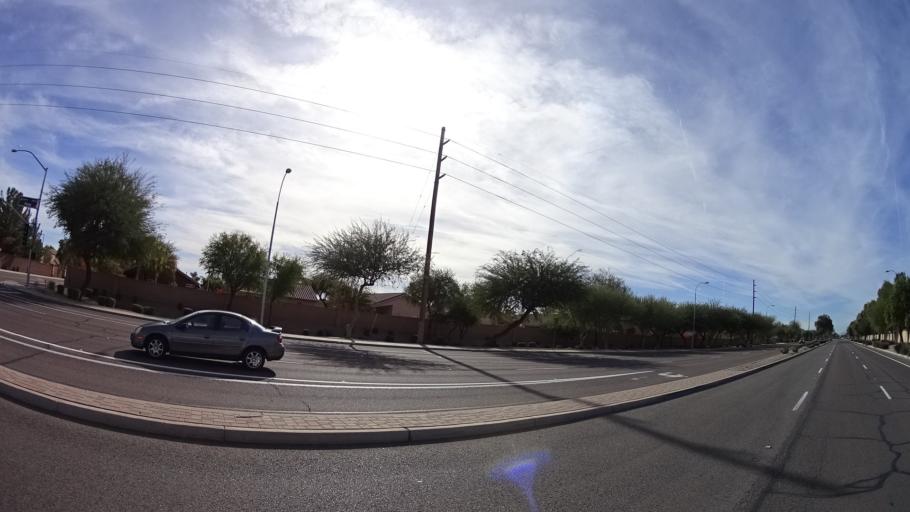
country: US
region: Arizona
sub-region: Maricopa County
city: Chandler
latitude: 33.2919
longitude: -111.7984
